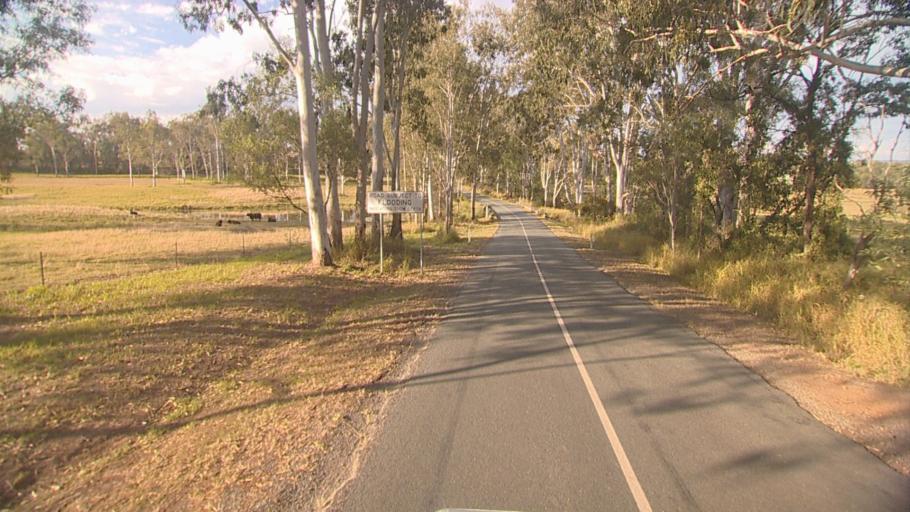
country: AU
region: Queensland
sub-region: Logan
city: Cedar Vale
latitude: -27.8496
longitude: 153.1366
